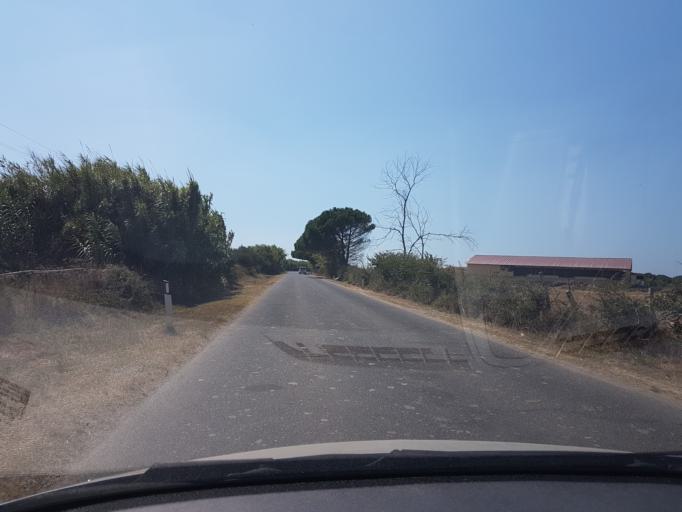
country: IT
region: Sardinia
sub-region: Provincia di Oristano
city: Riola Sardo
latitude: 40.0008
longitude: 8.5221
